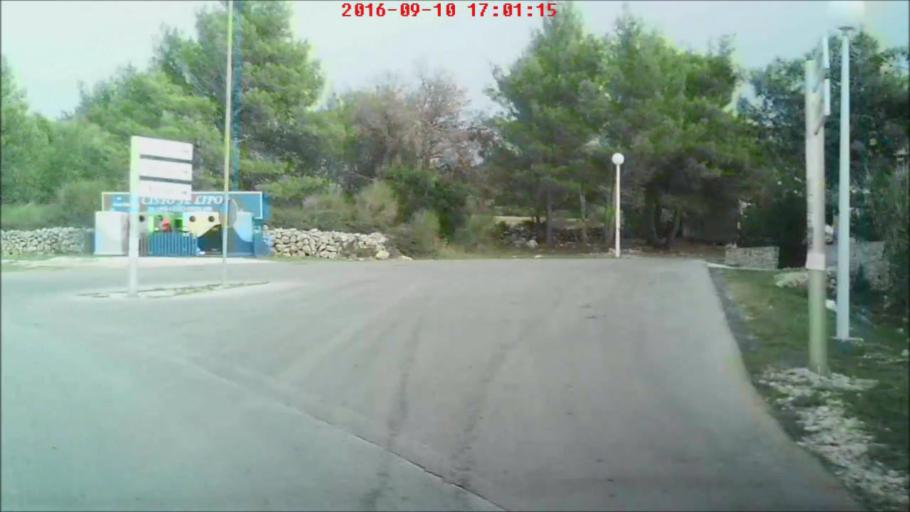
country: HR
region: Zadarska
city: Vir
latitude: 44.3067
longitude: 15.0572
